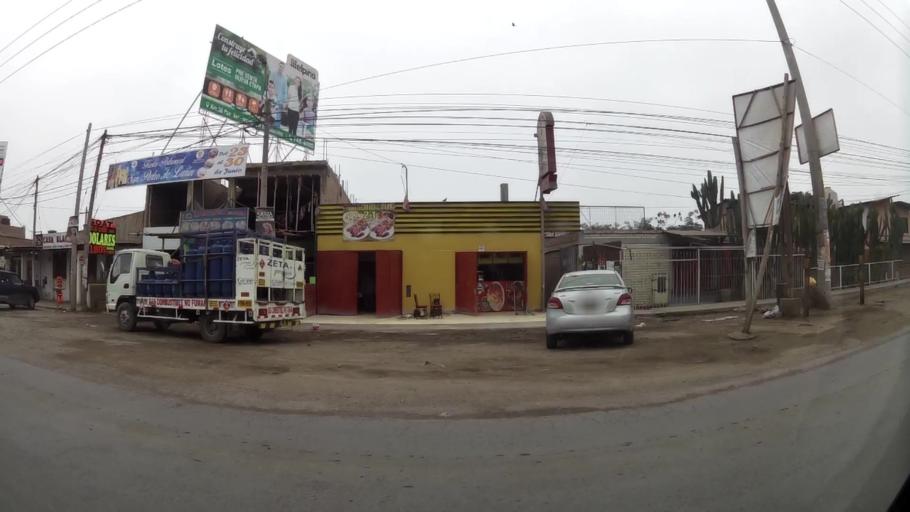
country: PE
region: Lima
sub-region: Lima
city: Punta Hermosa
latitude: -12.2607
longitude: -76.8839
